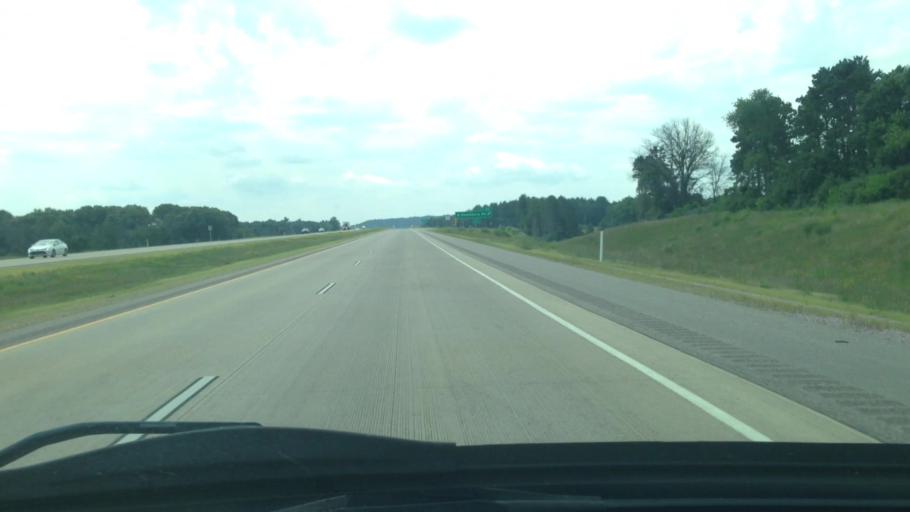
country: US
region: Wisconsin
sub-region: Sauk County
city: Lake Delton
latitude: 43.5391
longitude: -89.7873
